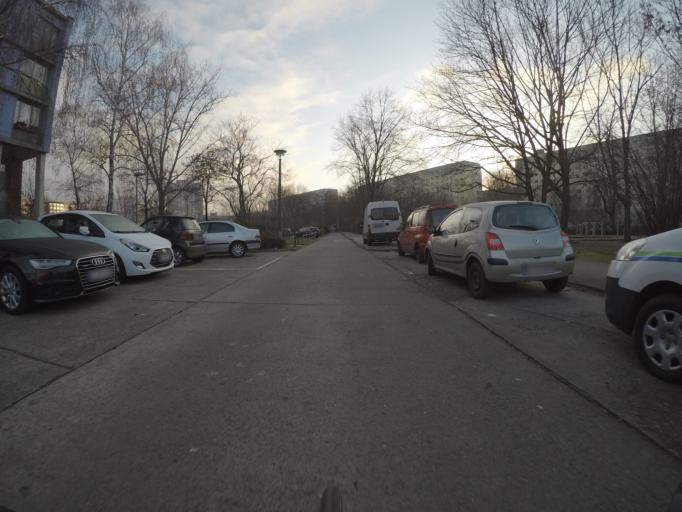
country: DE
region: Berlin
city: Friedrichsfelde
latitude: 52.4946
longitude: 13.5100
